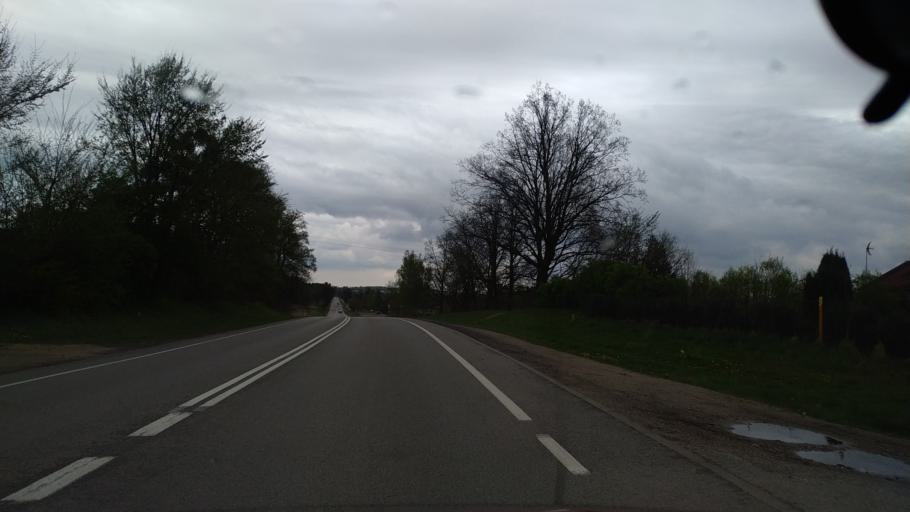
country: PL
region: Pomeranian Voivodeship
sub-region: Powiat tczewski
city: Pelplin
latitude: 54.0219
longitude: 18.6355
